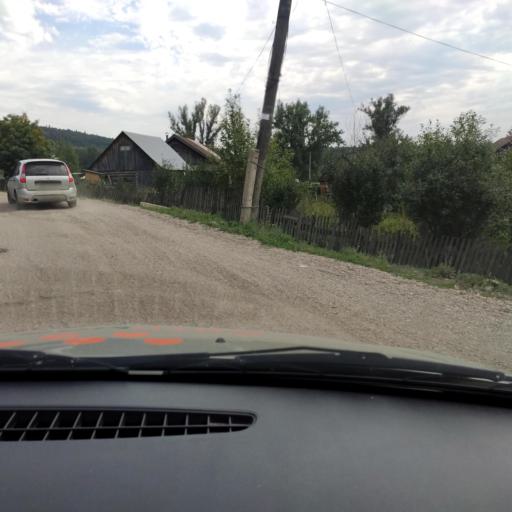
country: RU
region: Bashkortostan
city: Krasnyy Klyuch
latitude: 55.3808
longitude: 56.6745
